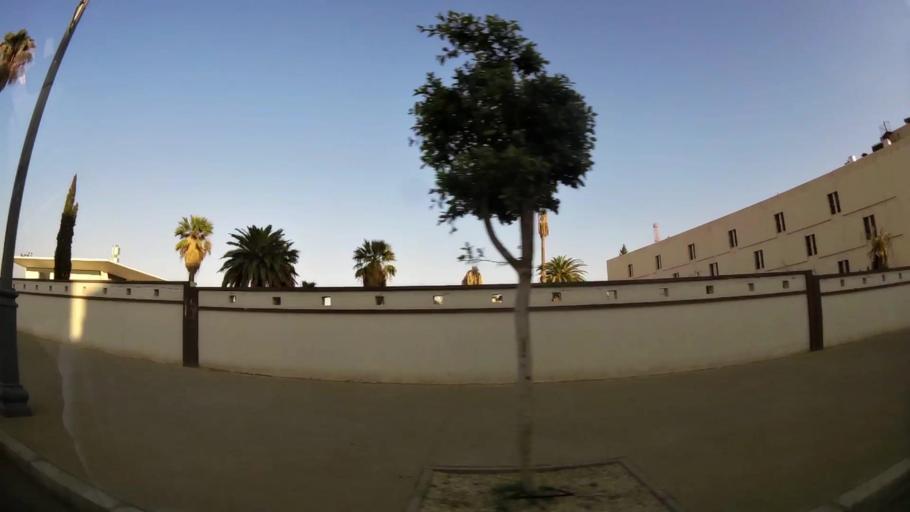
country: MA
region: Oriental
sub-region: Oujda-Angad
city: Oujda
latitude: 34.6800
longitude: -1.9230
